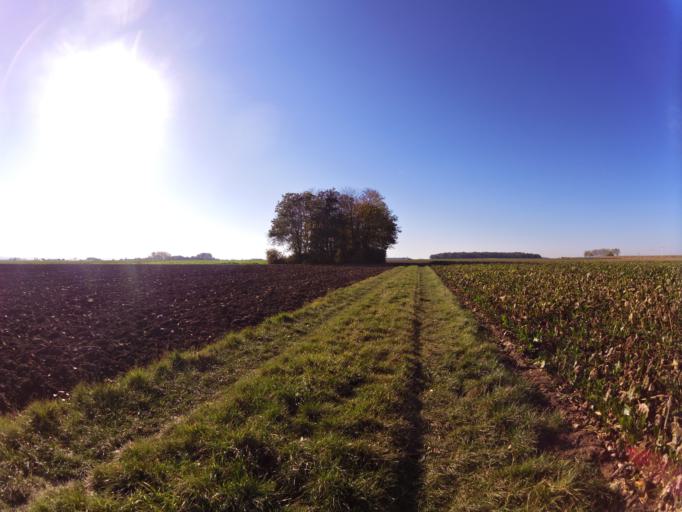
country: DE
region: Bavaria
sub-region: Regierungsbezirk Unterfranken
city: Giebelstadt
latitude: 49.6704
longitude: 9.9347
